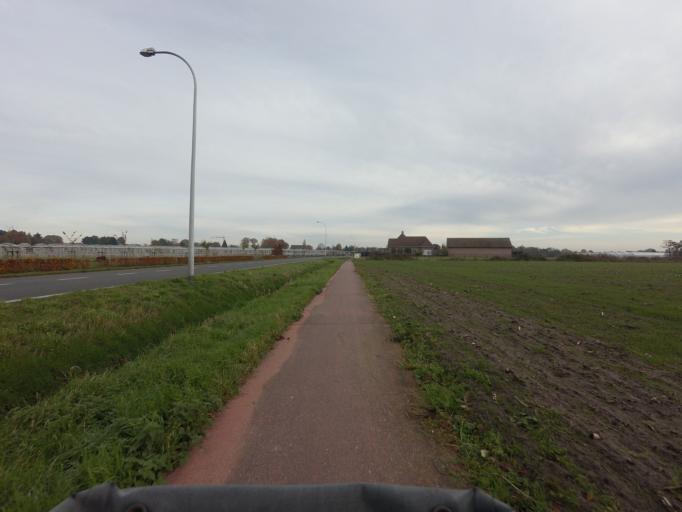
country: BE
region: Flanders
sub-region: Provincie Antwerpen
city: Hoogstraten
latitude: 51.4776
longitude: 4.7903
